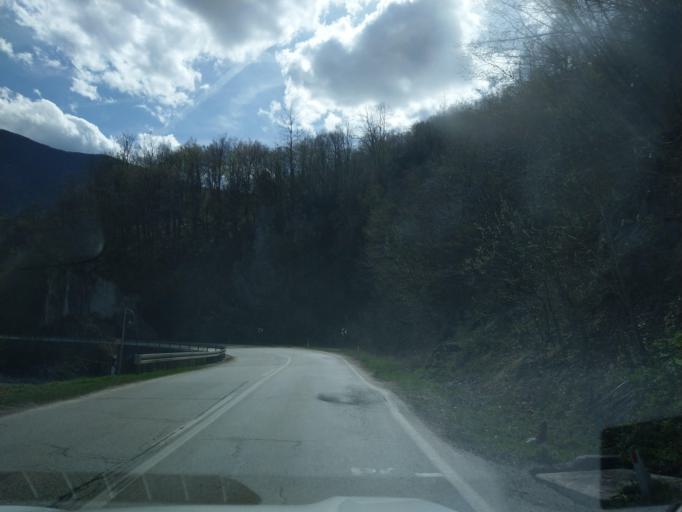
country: RS
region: Central Serbia
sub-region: Zlatiborski Okrug
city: Arilje
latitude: 43.6698
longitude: 20.1013
